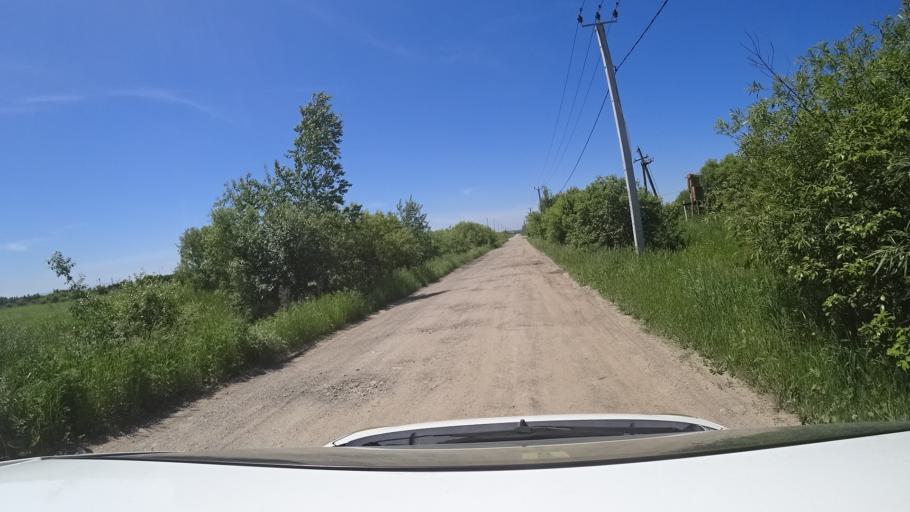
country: RU
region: Khabarovsk Krai
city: Topolevo
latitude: 48.5006
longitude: 135.1942
